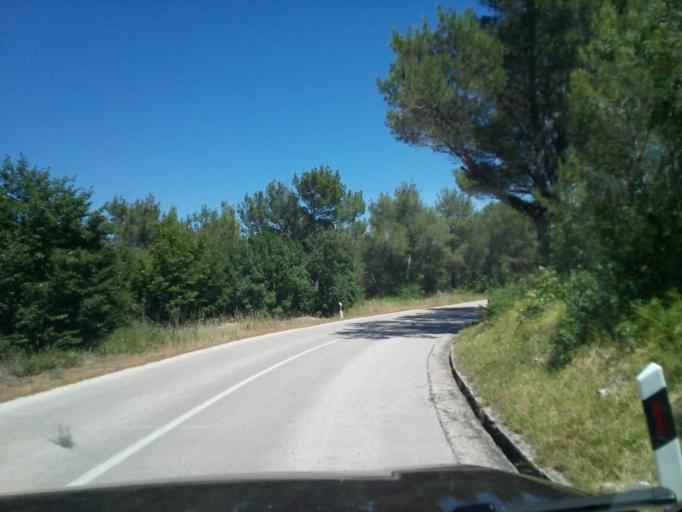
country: HR
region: Zadarska
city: Pridraga
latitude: 44.1810
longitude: 15.5403
